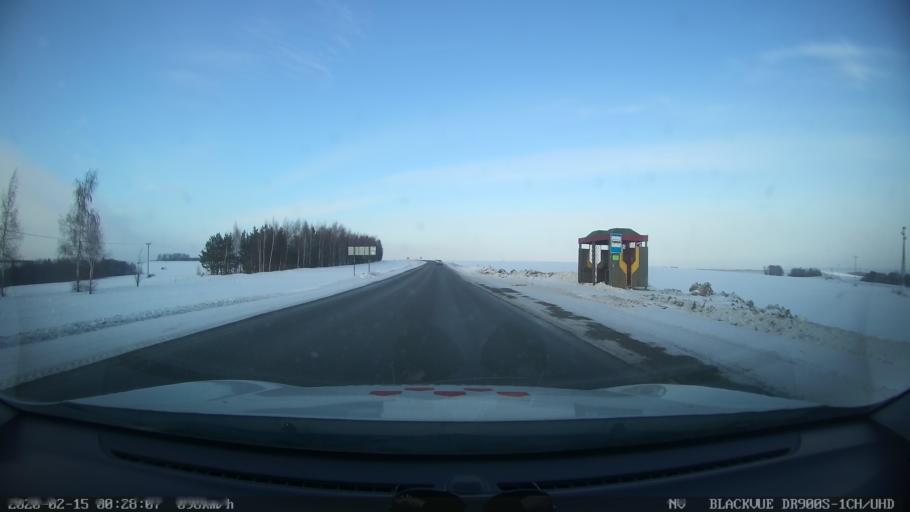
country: RU
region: Tatarstan
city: Verkhniy Uslon
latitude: 55.6378
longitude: 48.8738
